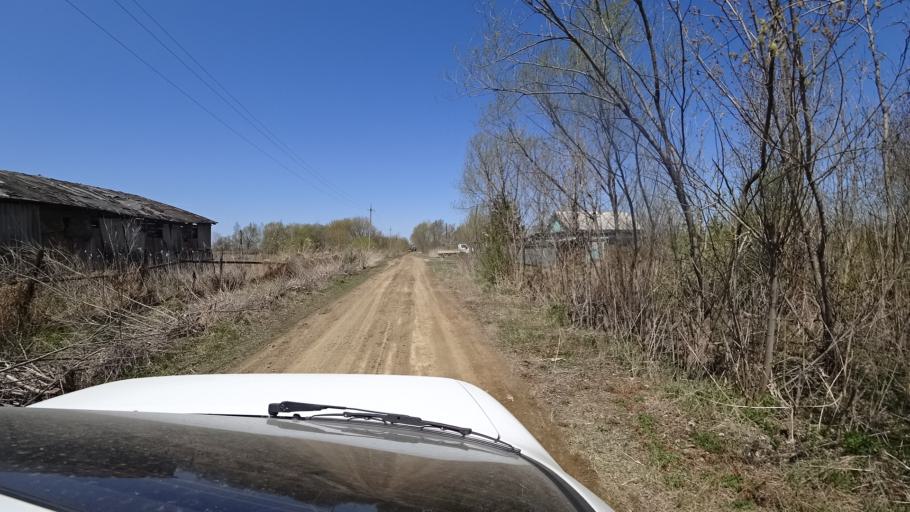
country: RU
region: Primorskiy
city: Lazo
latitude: 45.7988
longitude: 133.7612
